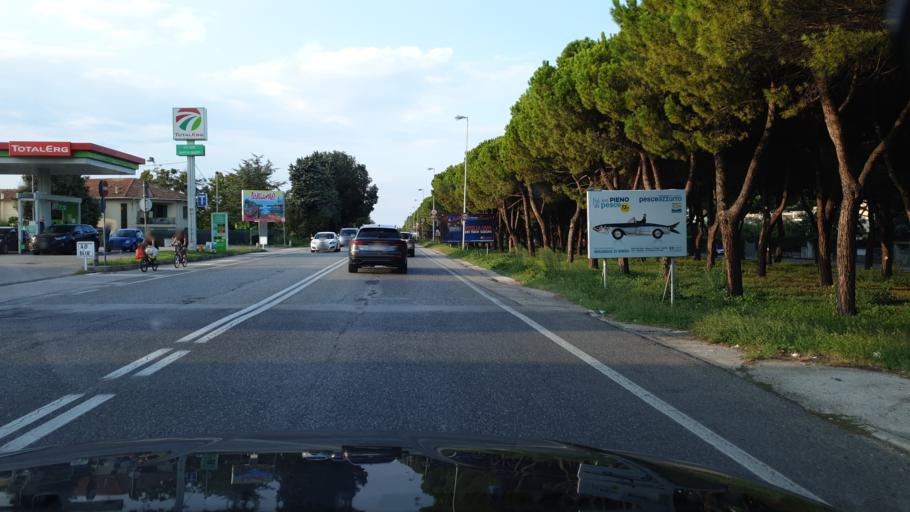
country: IT
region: Emilia-Romagna
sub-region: Provincia di Rimini
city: Riccione
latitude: 44.0054
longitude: 12.6338
